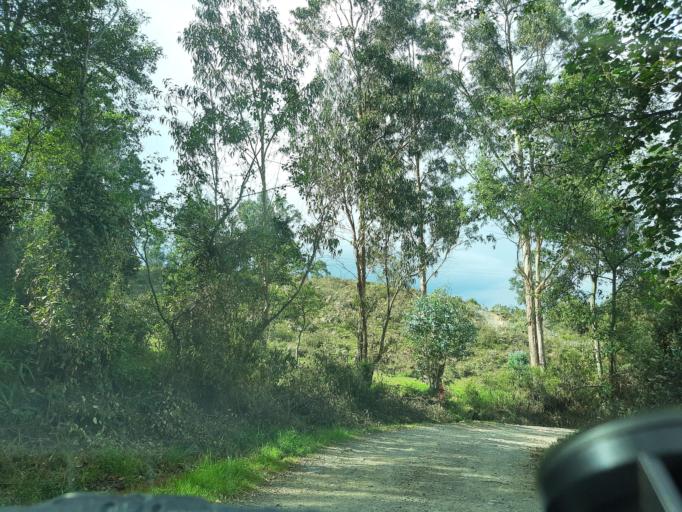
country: CO
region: Boyaca
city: Raquira
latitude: 5.5235
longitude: -73.6664
